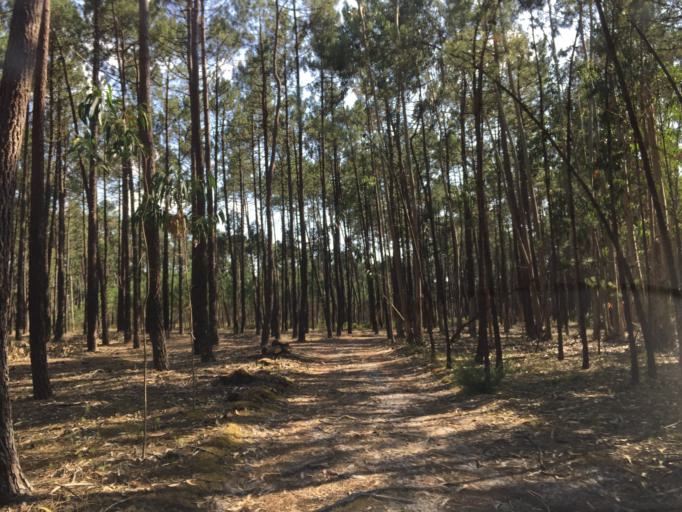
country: PT
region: Leiria
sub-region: Leiria
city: Monte Redondo
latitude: 39.9561
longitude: -8.8208
